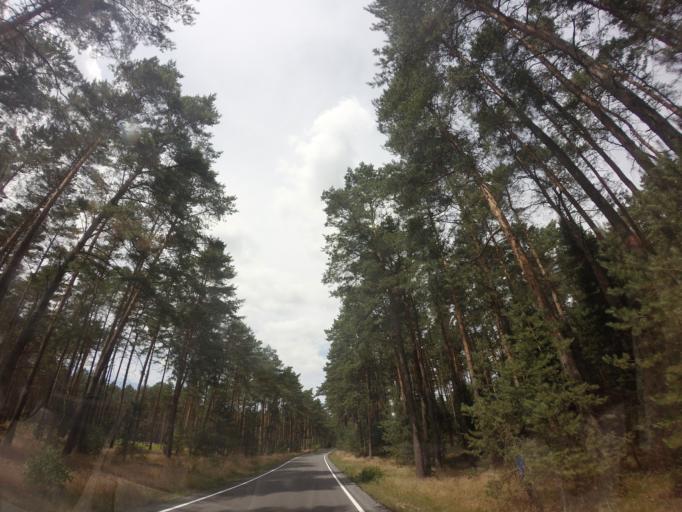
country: PL
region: West Pomeranian Voivodeship
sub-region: Powiat choszczenski
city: Drawno
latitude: 53.1319
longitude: 15.7213
